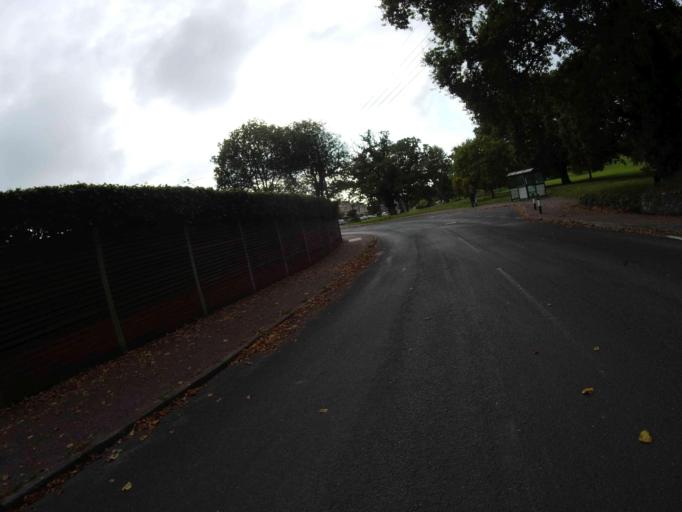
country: GB
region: England
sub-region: Devon
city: Budleigh Salterton
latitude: 50.6335
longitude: -3.3293
